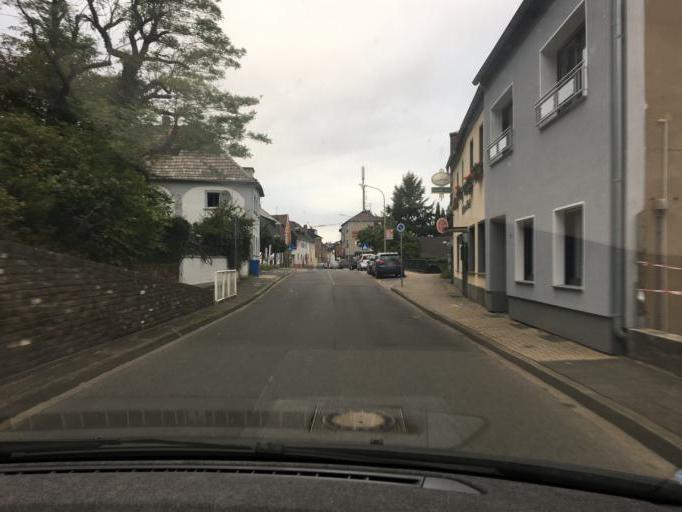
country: DE
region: North Rhine-Westphalia
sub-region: Regierungsbezirk Koln
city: Kreuzau
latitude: 50.7646
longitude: 6.4786
